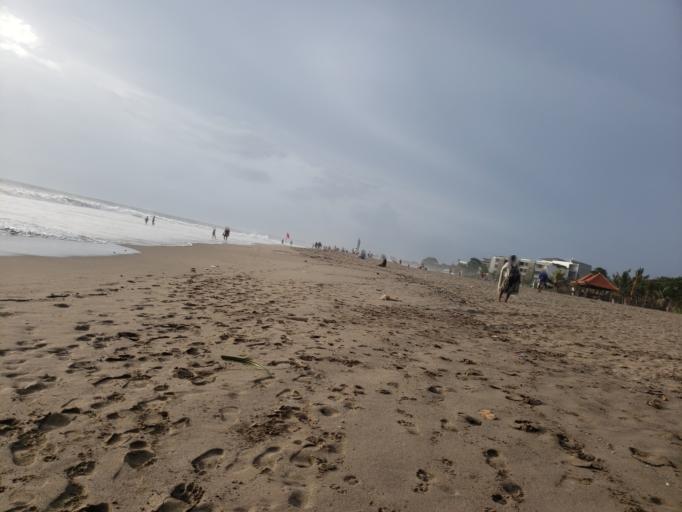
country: ID
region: Bali
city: Kuta
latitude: -8.6834
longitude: 115.1517
